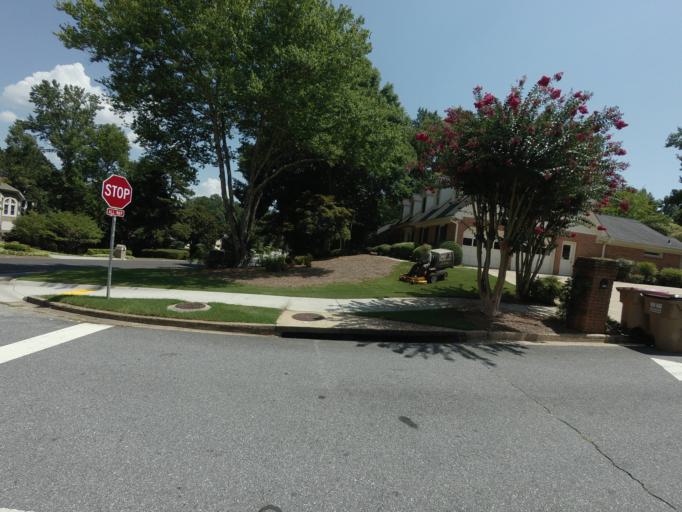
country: US
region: Georgia
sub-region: Fulton County
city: Johns Creek
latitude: 34.0350
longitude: -84.2036
